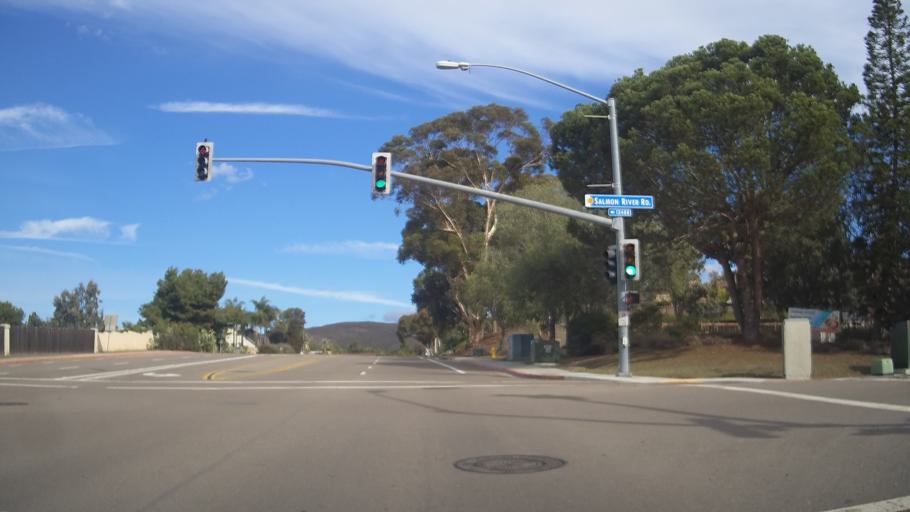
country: US
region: California
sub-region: San Diego County
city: Fairbanks Ranch
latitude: 32.9598
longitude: -117.1228
